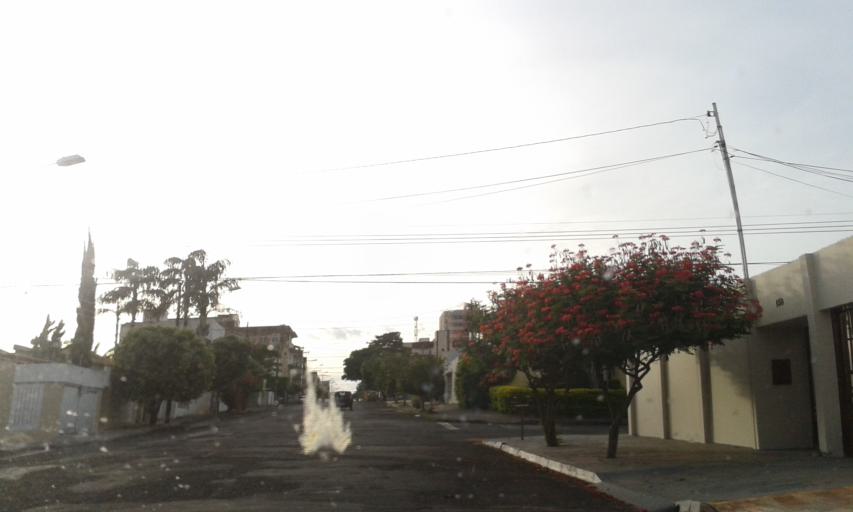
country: BR
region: Minas Gerais
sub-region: Uberlandia
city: Uberlandia
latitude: -18.9213
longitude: -48.2522
